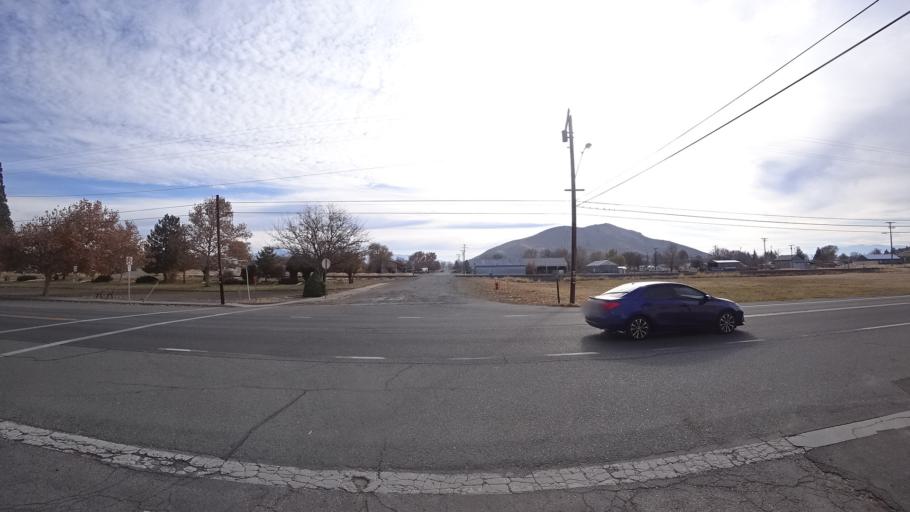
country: US
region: California
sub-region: Siskiyou County
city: Montague
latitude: 41.7270
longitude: -122.5286
